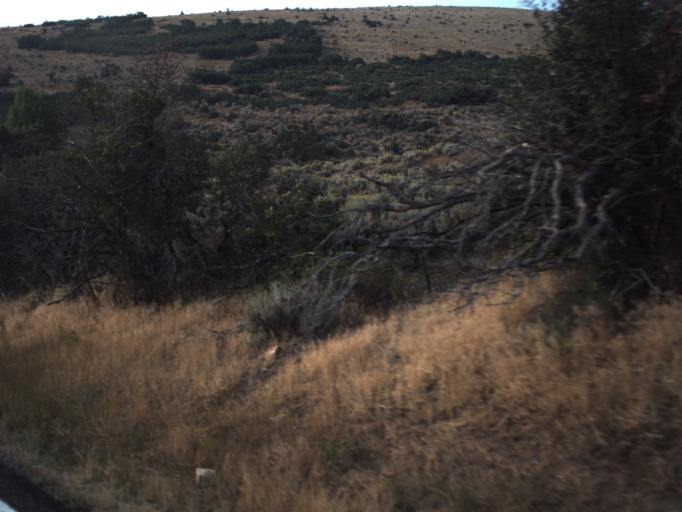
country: US
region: Utah
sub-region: Summit County
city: Kamas
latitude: 40.6413
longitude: -111.2662
